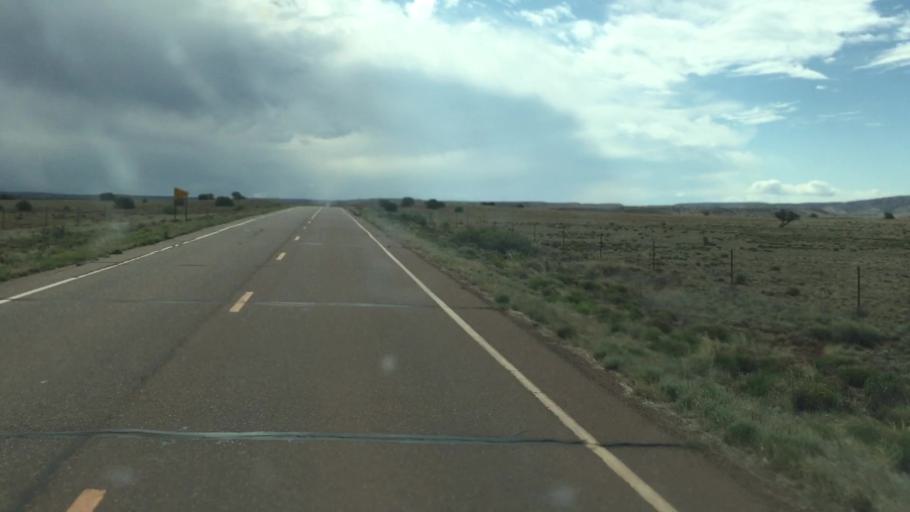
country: US
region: Arizona
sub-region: Apache County
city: Saint Johns
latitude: 34.5115
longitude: -109.6883
